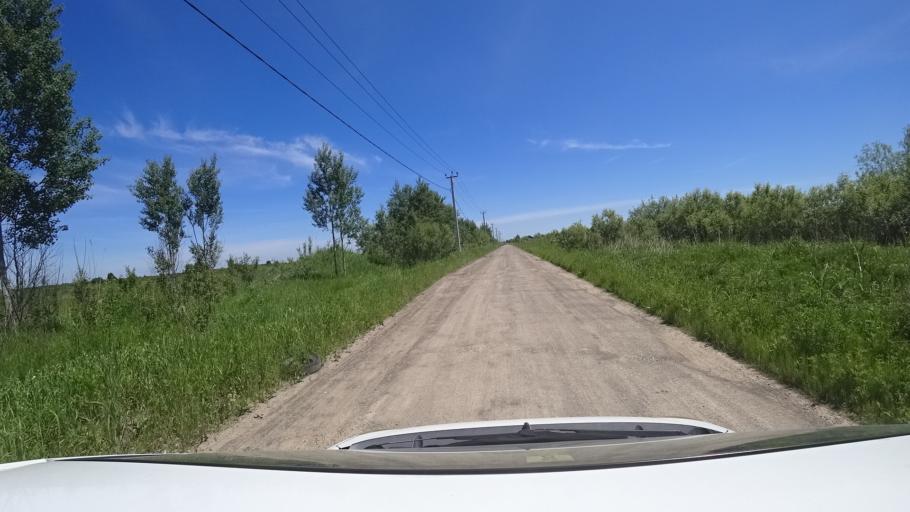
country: RU
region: Khabarovsk Krai
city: Topolevo
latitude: 48.4999
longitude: 135.2000
